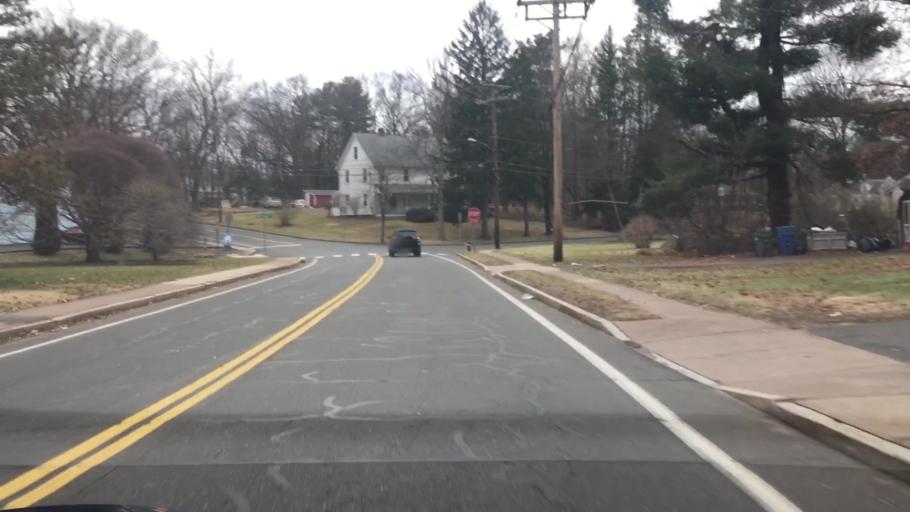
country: US
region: Connecticut
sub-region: Hartford County
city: Manchester
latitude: 41.7910
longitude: -72.5362
